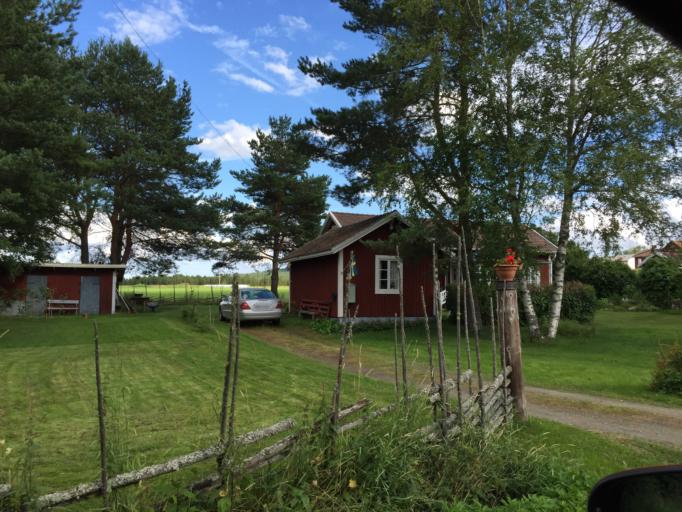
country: SE
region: Gaevleborg
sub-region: Ljusdals Kommun
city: Jaervsoe
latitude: 61.7556
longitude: 16.1678
